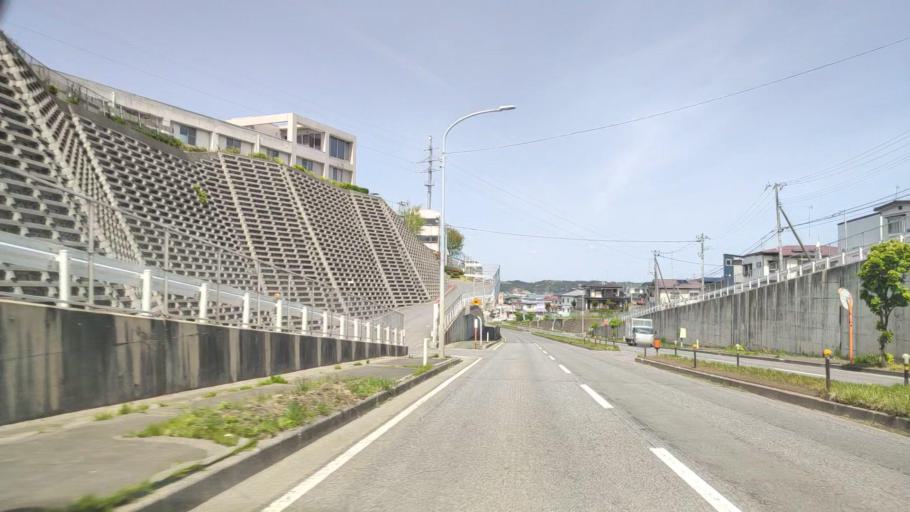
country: JP
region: Aomori
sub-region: Hachinohe Shi
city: Uchimaru
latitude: 40.4995
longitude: 141.4562
